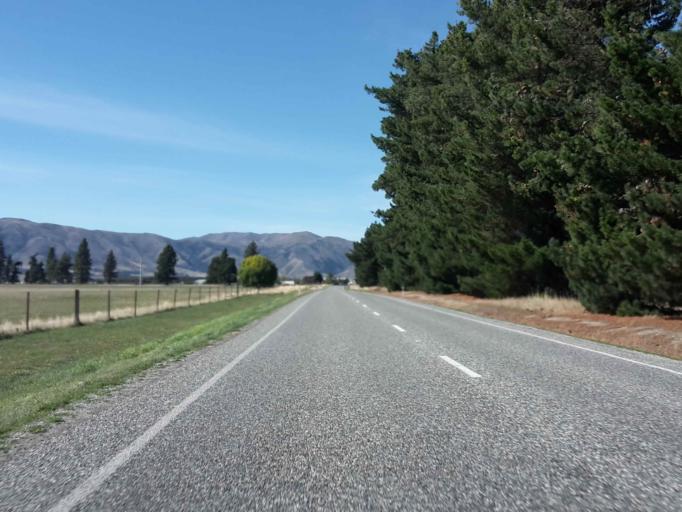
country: NZ
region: Otago
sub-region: Queenstown-Lakes District
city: Wanaka
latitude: -44.7211
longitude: 169.2306
